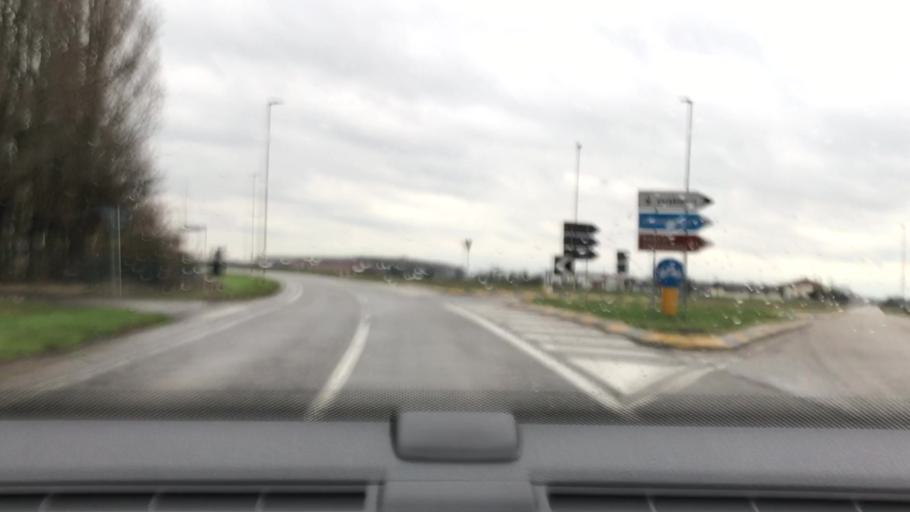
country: IT
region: Lombardy
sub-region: Provincia di Cremona
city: Torricella del Pizzo
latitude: 45.0291
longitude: 10.3099
